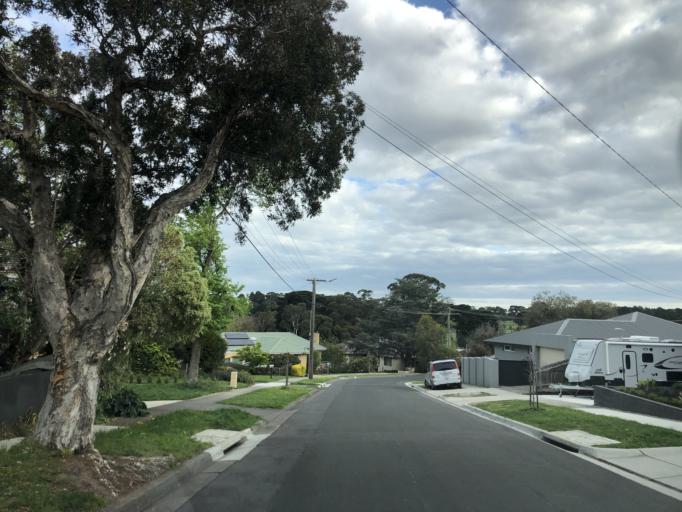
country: AU
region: Victoria
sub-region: Monash
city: Ashwood
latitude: -37.8671
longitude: 145.1176
